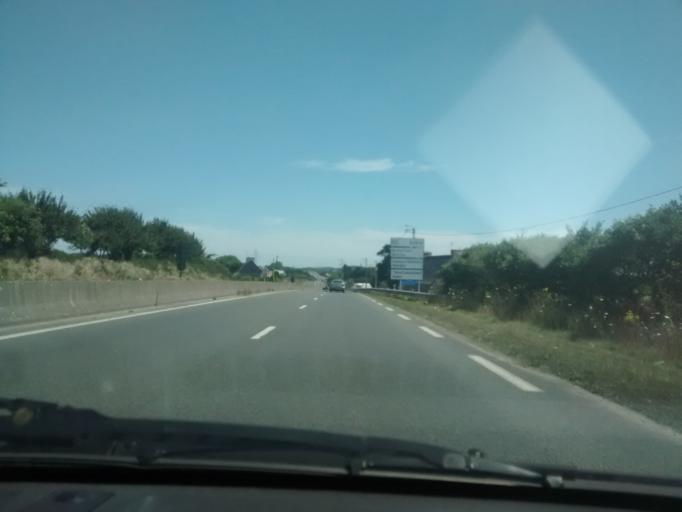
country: FR
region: Brittany
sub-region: Departement des Cotes-d'Armor
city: Ploubezre
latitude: 48.7227
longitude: -3.4272
